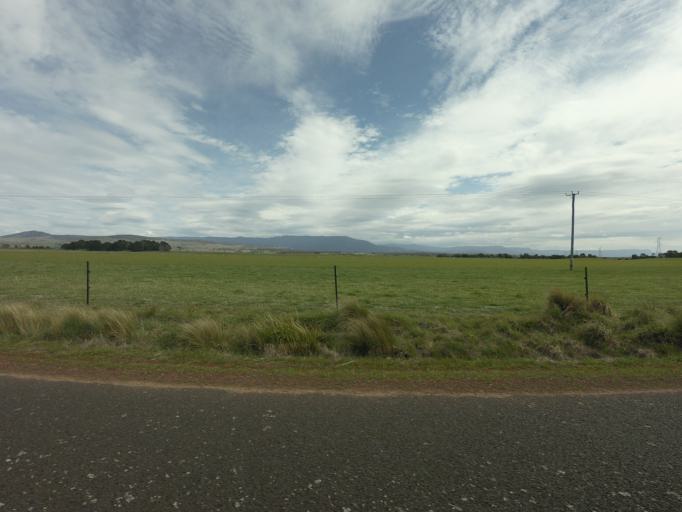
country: AU
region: Tasmania
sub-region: Northern Midlands
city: Evandale
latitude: -41.8495
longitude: 147.3388
